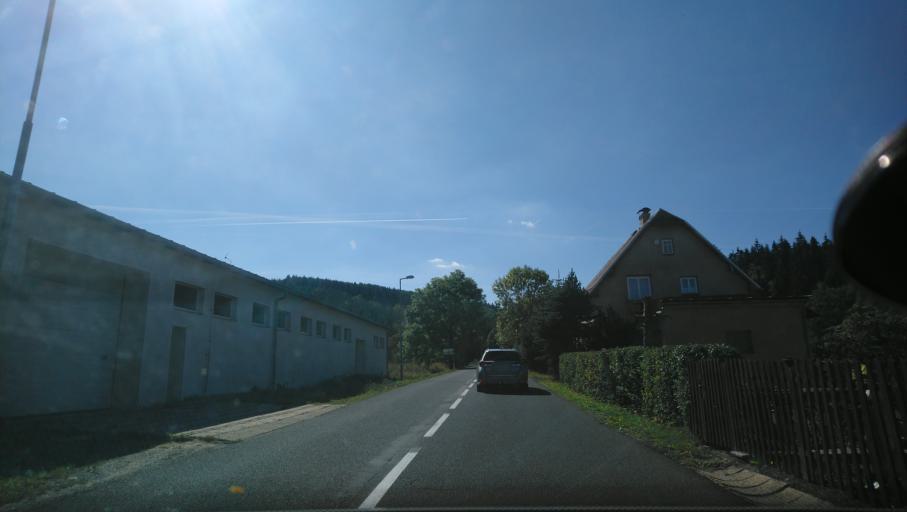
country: CZ
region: Ustecky
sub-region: Okres Chomutov
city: Kovarska
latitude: 50.4391
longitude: 13.0155
